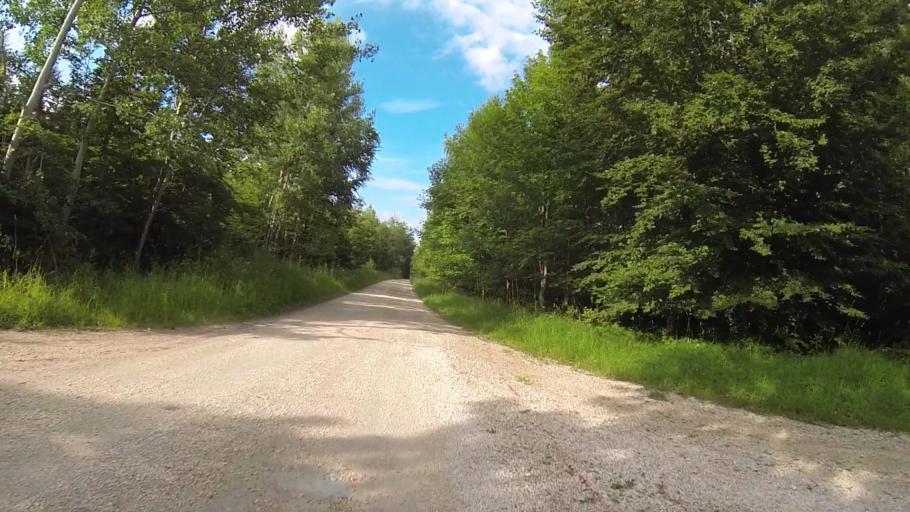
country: DE
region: Baden-Wuerttemberg
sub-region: Regierungsbezirk Stuttgart
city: Nattheim
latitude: 48.7182
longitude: 10.2733
